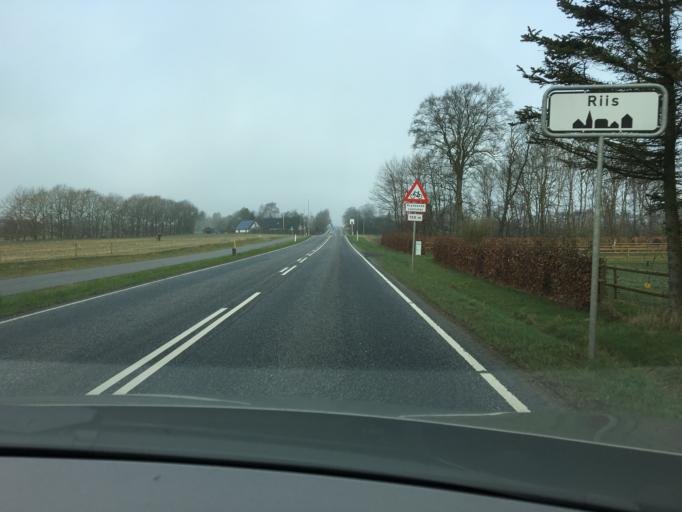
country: DK
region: South Denmark
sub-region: Vejle Kommune
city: Give
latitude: 55.8264
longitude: 9.3264
